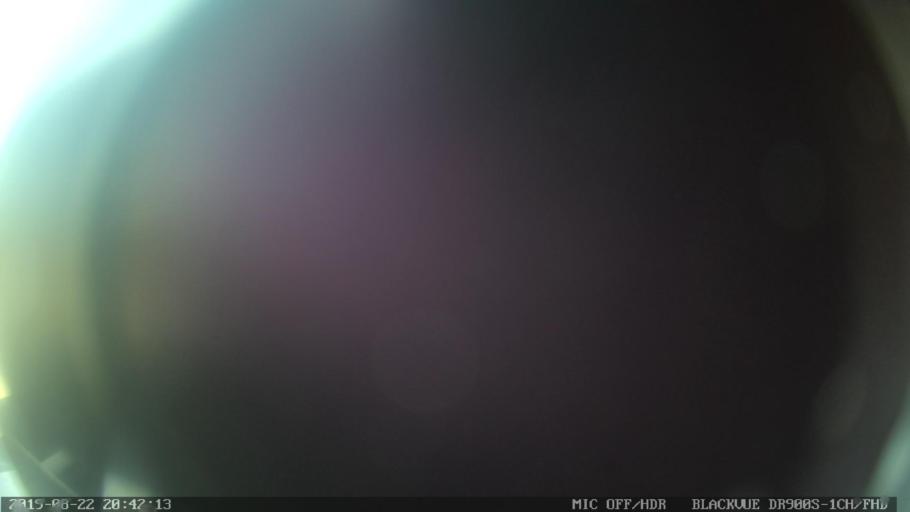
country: PT
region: Castelo Branco
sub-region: Proenca-A-Nova
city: Proenca-a-Nova
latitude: 39.6927
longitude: -7.8137
